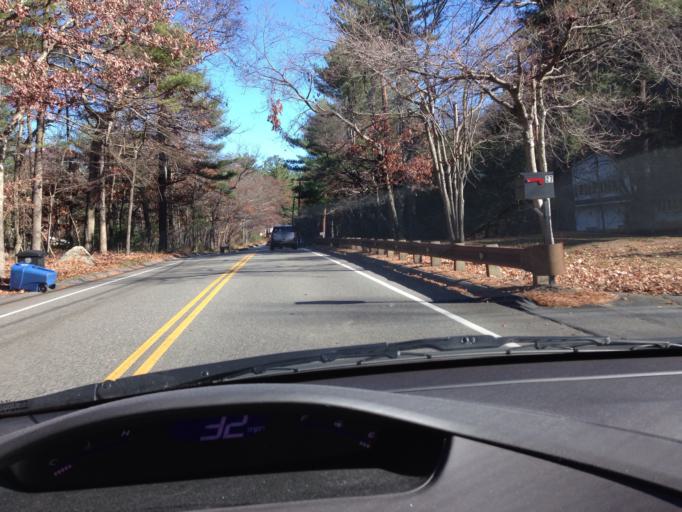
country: US
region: Massachusetts
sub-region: Middlesex County
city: Bedford
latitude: 42.4989
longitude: -71.2550
